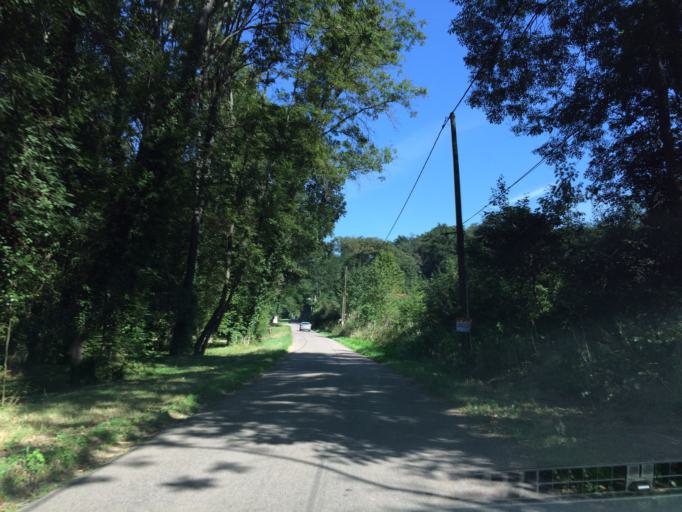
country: FR
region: Bourgogne
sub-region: Departement de l'Yonne
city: Fleury-la-Vallee
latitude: 47.8505
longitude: 3.3997
